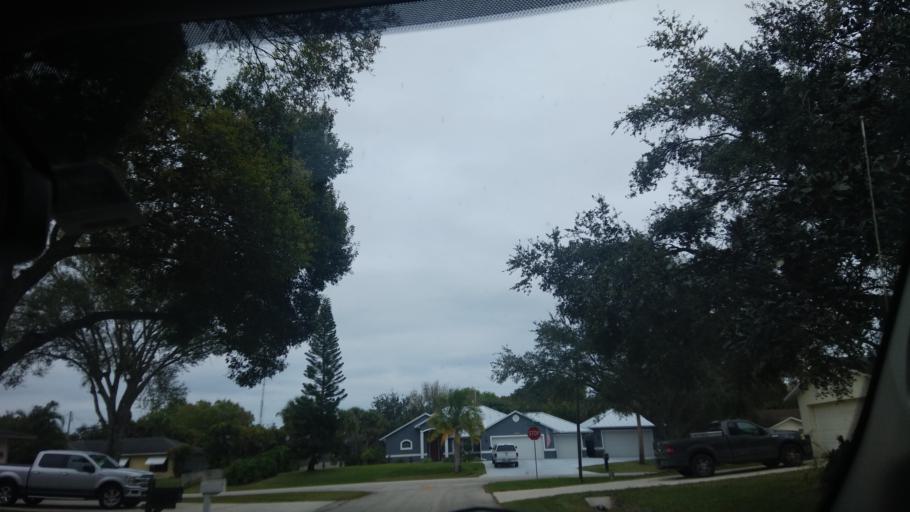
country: US
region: Florida
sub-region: Indian River County
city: Sebastian
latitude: 27.7642
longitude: -80.4855
